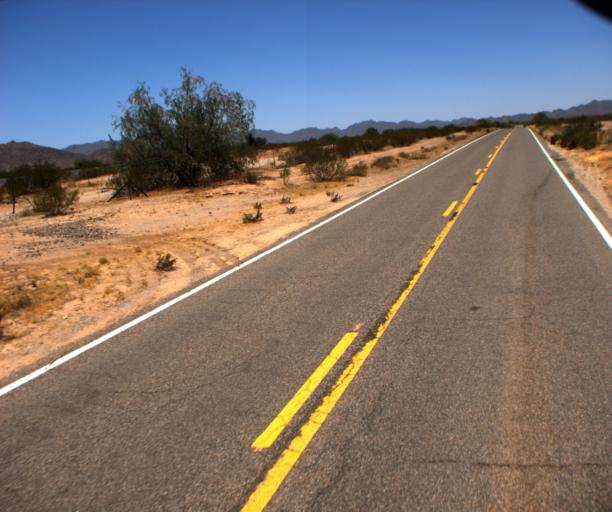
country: US
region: Arizona
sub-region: Pinal County
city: Maricopa
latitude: 33.0337
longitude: -112.3558
